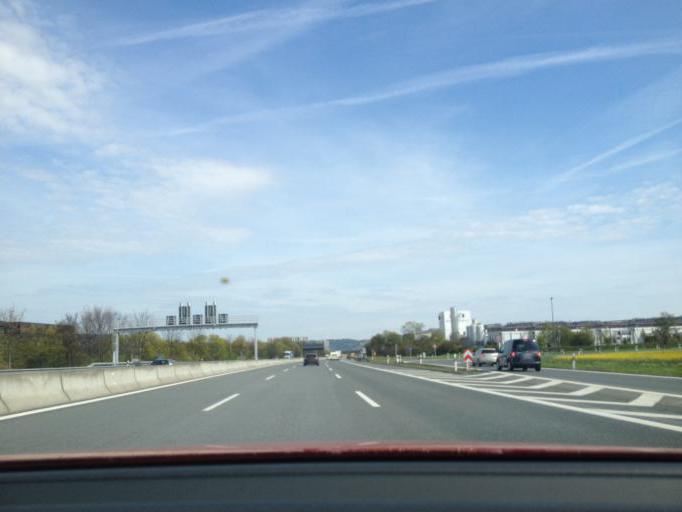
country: DE
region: Bavaria
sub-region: Upper Franconia
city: Bindlach
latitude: 49.9622
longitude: 11.6055
